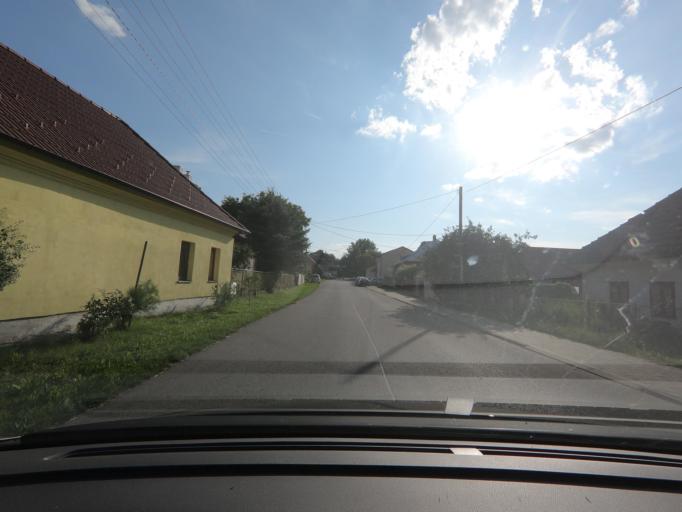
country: SK
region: Nitriansky
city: Stara Tura
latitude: 48.7358
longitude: 17.7066
